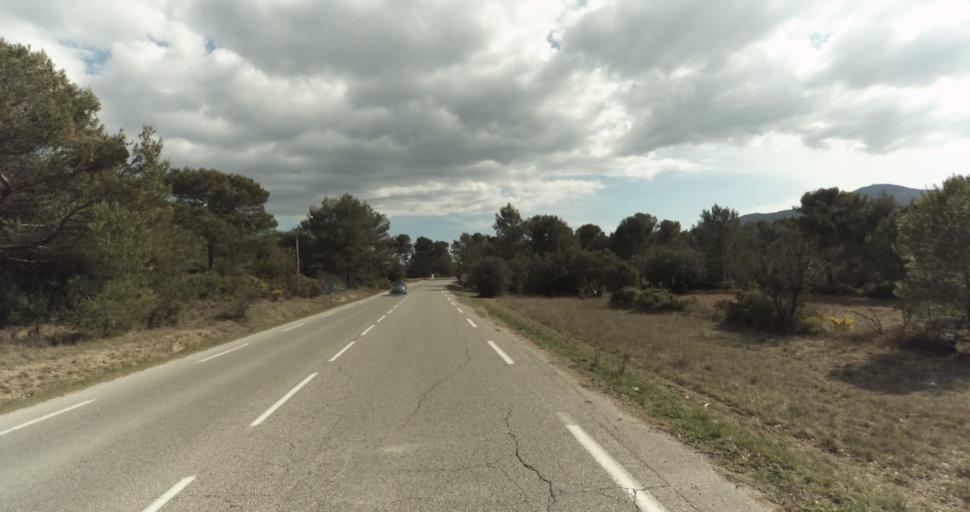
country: FR
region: Provence-Alpes-Cote d'Azur
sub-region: Departement des Bouches-du-Rhone
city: Greasque
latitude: 43.4417
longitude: 5.5284
